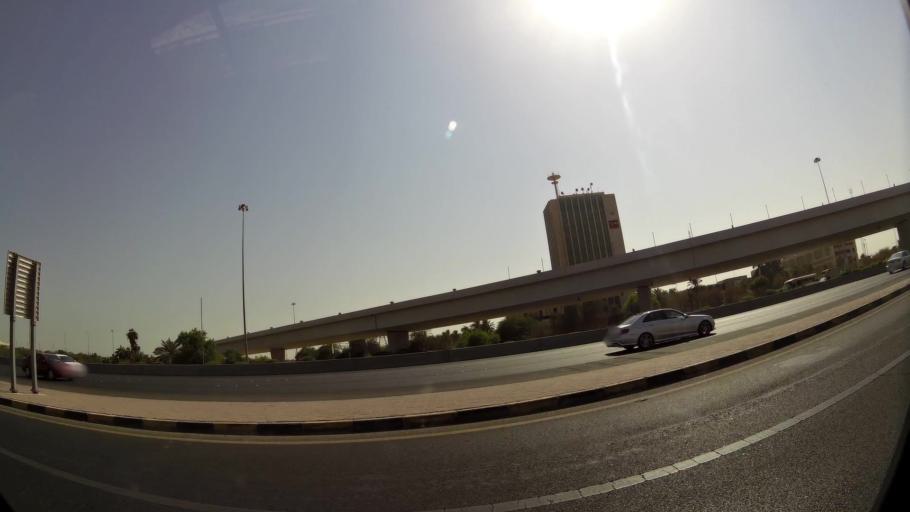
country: KW
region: Muhafazat Hawalli
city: Hawalli
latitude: 29.3074
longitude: 48.0206
